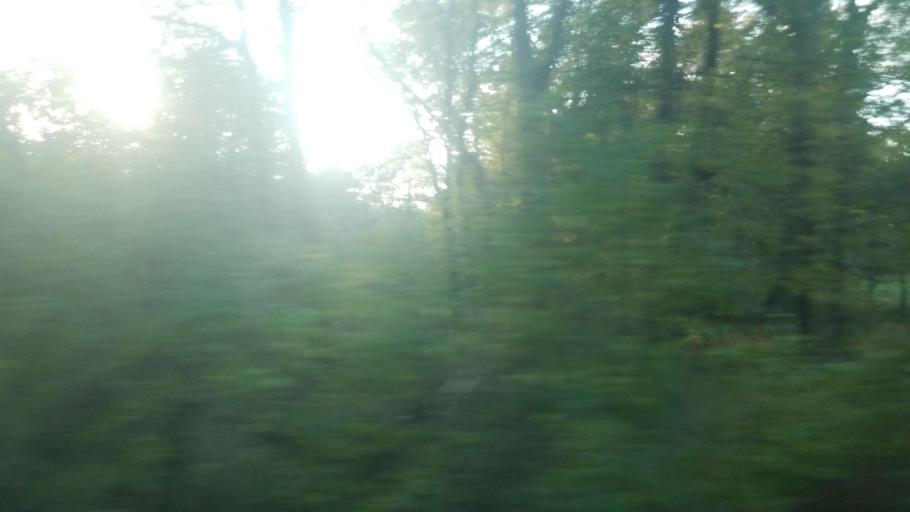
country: US
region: Illinois
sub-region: Williamson County
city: Marion
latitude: 37.7652
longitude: -88.8082
